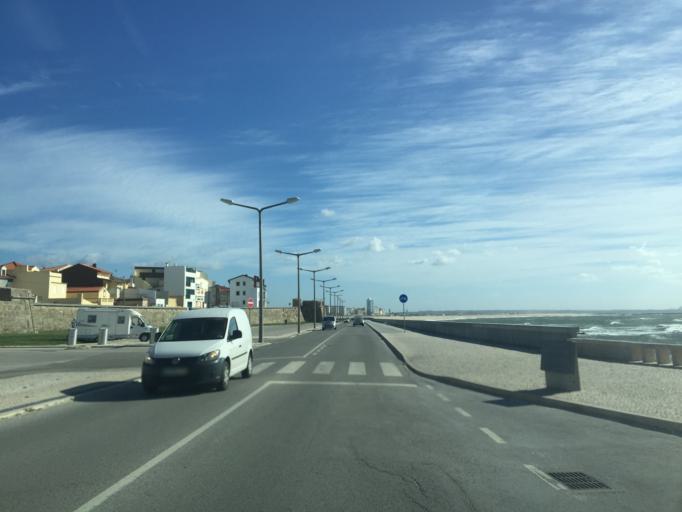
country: PT
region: Coimbra
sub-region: Figueira da Foz
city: Buarcos
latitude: 40.1660
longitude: -8.8817
